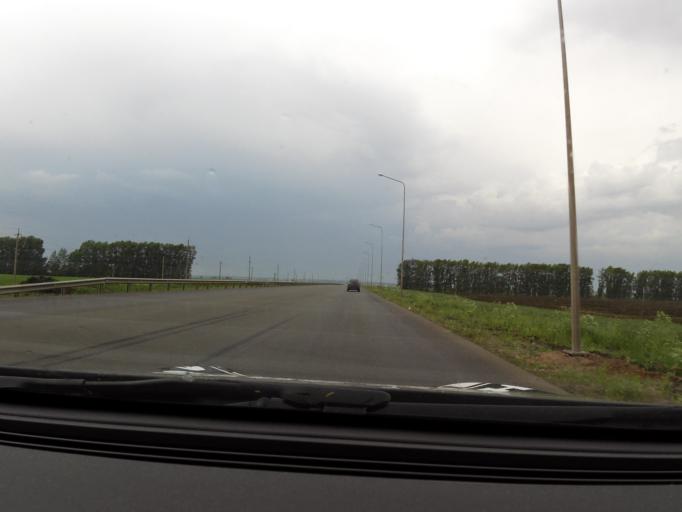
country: RU
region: Bashkortostan
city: Asanovo
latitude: 54.8880
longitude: 55.6671
